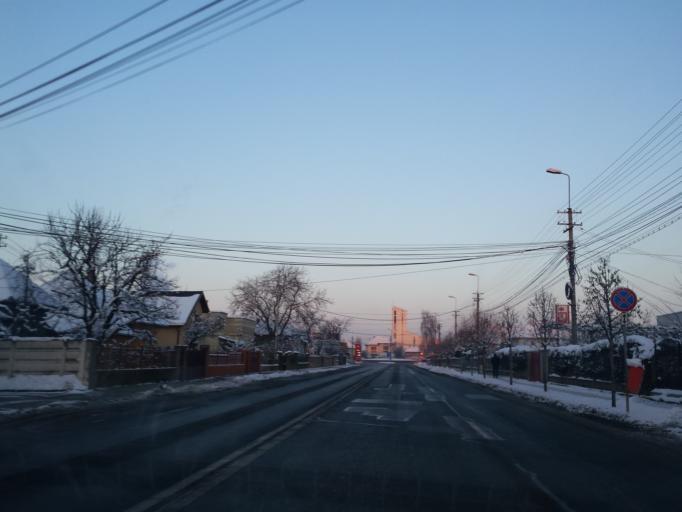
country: RO
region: Alba
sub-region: Municipiul Alba Iulia
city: Alba Iulia
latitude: 46.0731
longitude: 23.5680
